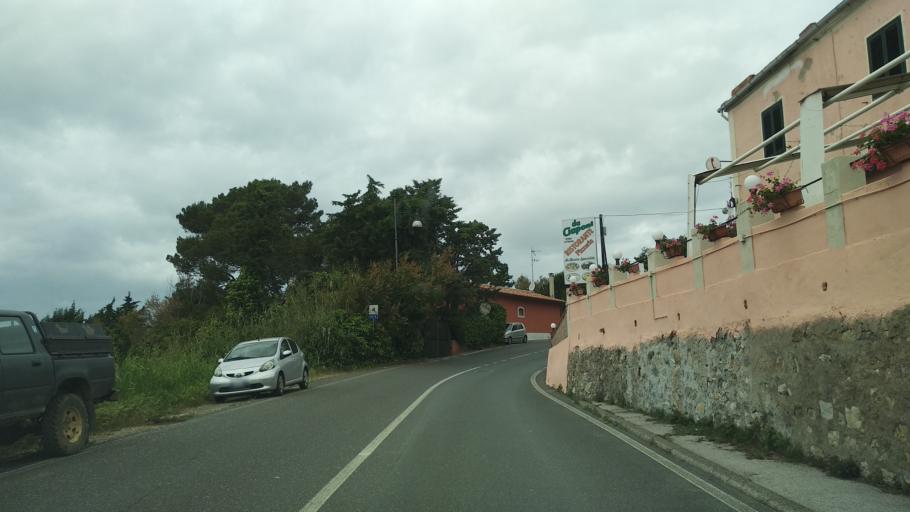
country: IT
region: Tuscany
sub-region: Provincia di Livorno
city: Quercianella
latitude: 43.4886
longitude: 10.3630
